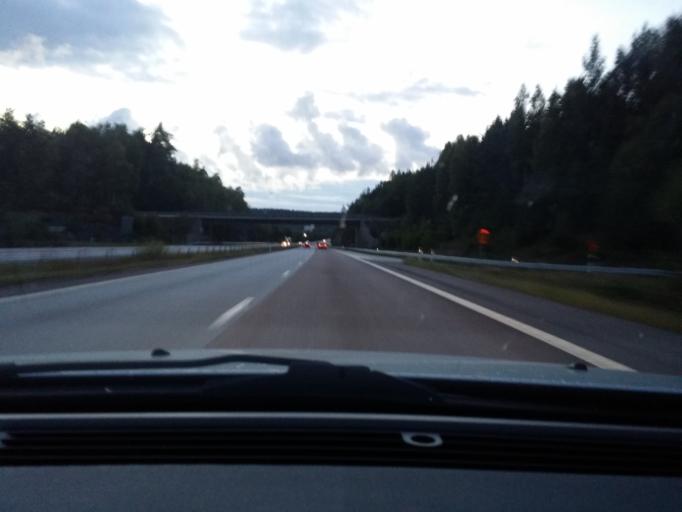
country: SE
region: Uppsala
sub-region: Habo Kommun
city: Balsta
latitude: 59.5653
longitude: 17.5628
